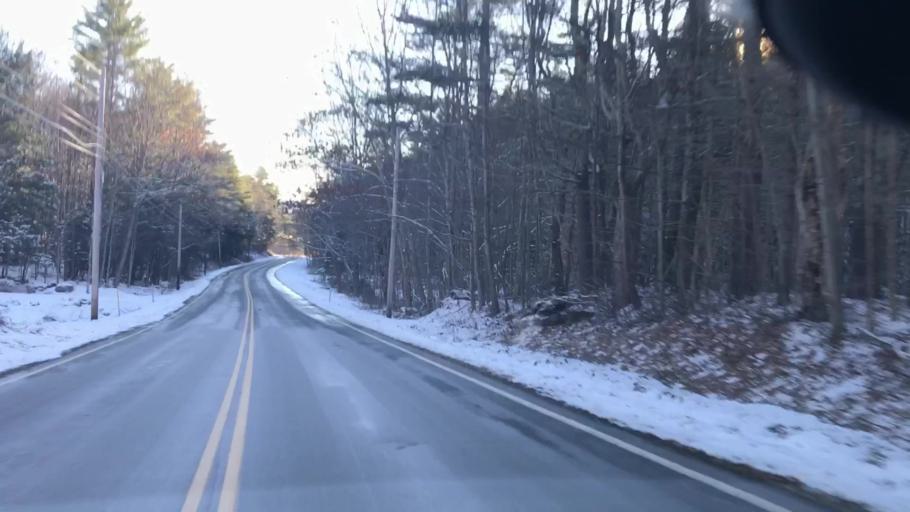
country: US
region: New Hampshire
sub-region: Grafton County
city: Haverhill
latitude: 43.9872
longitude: -72.0797
